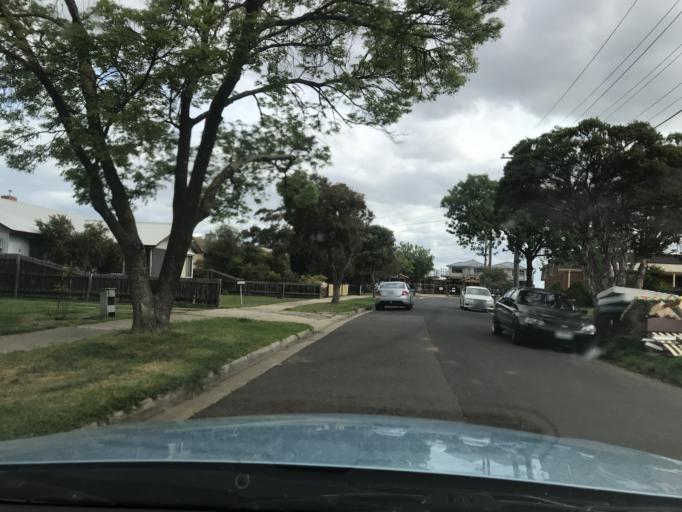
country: AU
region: Victoria
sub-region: Hobsons Bay
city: Laverton
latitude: -37.8544
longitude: 144.7720
